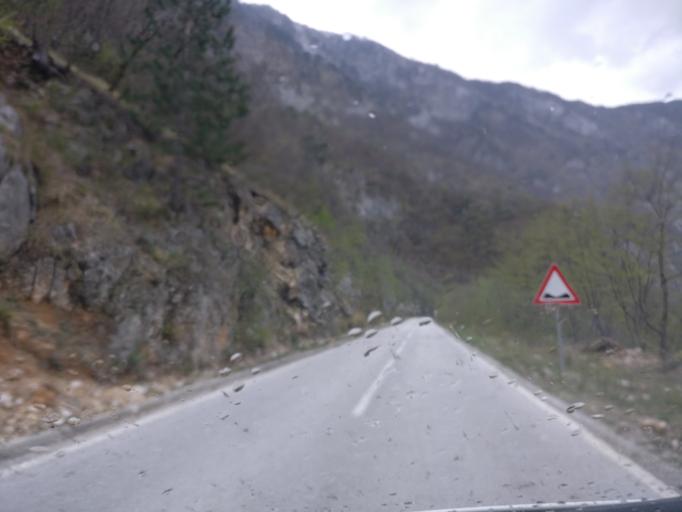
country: ME
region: Opstina Pluzine
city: Pluzine
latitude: 43.2179
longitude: 18.8545
